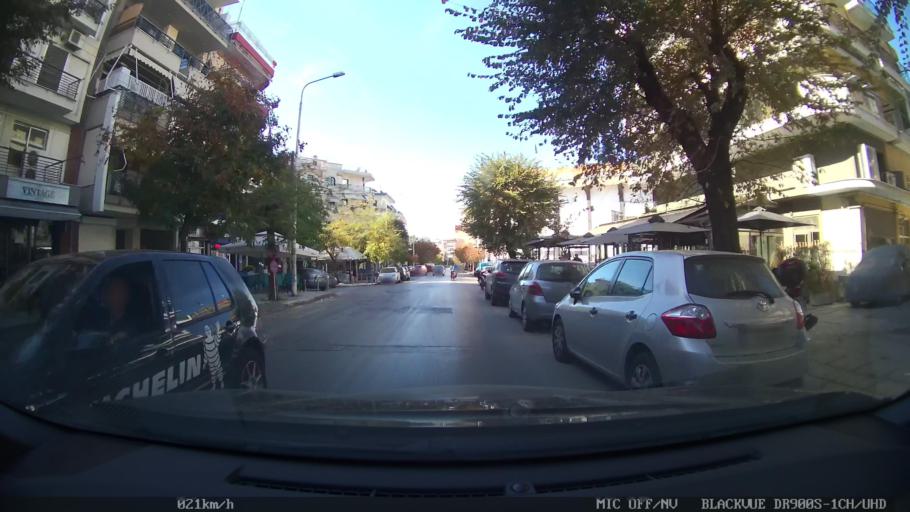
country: GR
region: Central Macedonia
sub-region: Nomos Thessalonikis
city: Triandria
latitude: 40.6124
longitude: 22.9735
